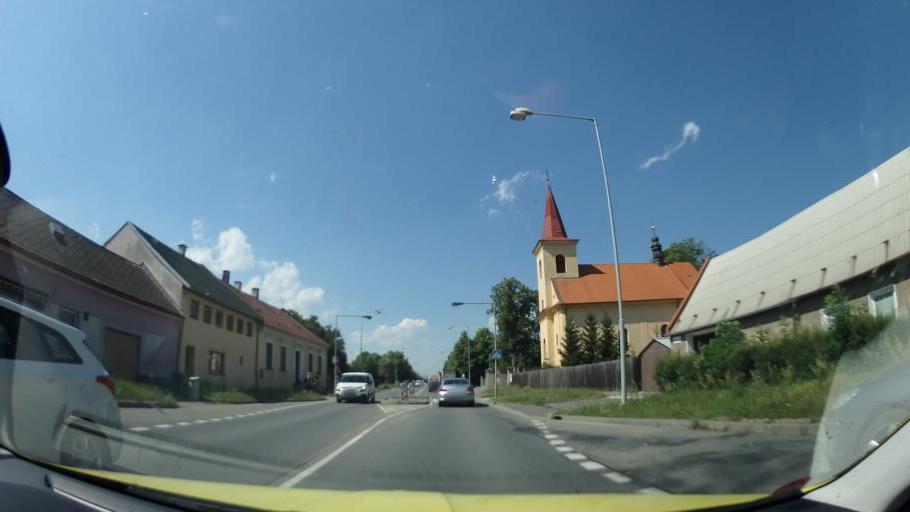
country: CZ
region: Olomoucky
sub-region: Okres Olomouc
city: Olomouc
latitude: 49.5680
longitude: 17.2613
